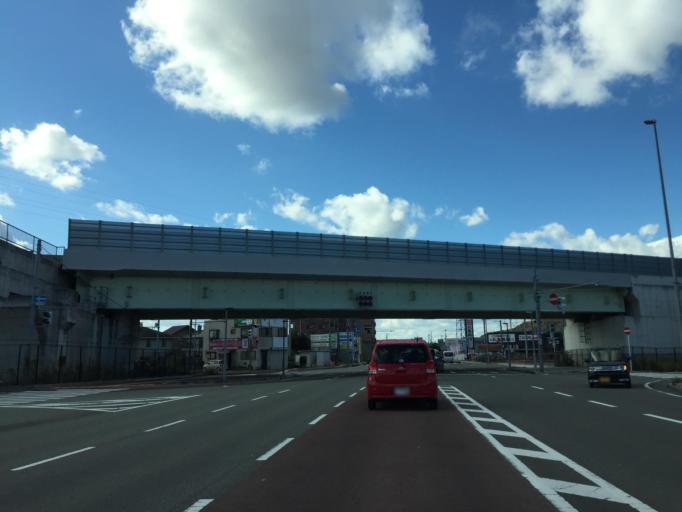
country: JP
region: Wakayama
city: Wakayama-shi
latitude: 34.2597
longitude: 135.1744
